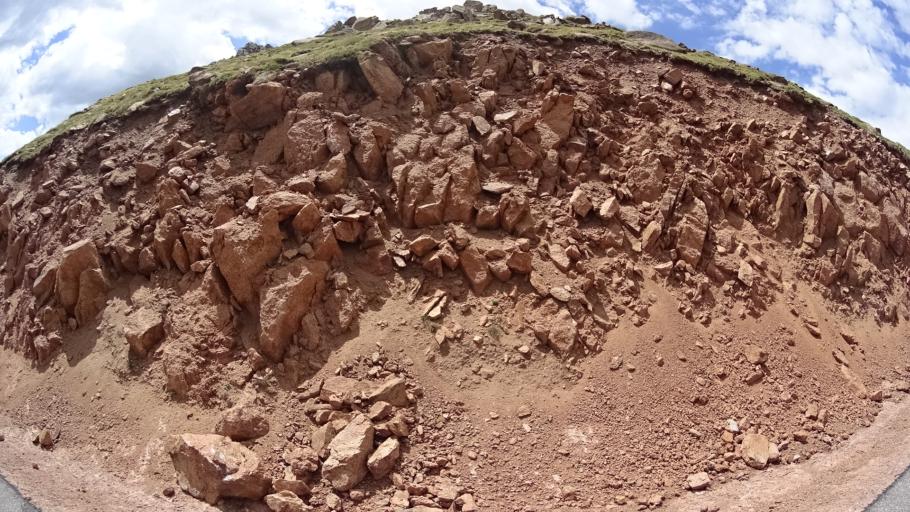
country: US
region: Colorado
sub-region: El Paso County
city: Cascade-Chipita Park
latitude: 38.8668
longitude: -105.0654
